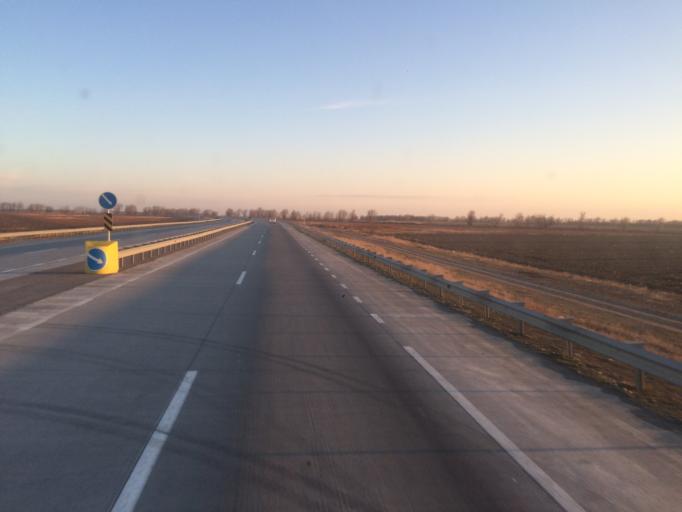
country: KZ
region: Ongtustik Qazaqstan
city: Turkestan
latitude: 43.1849
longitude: 68.4962
